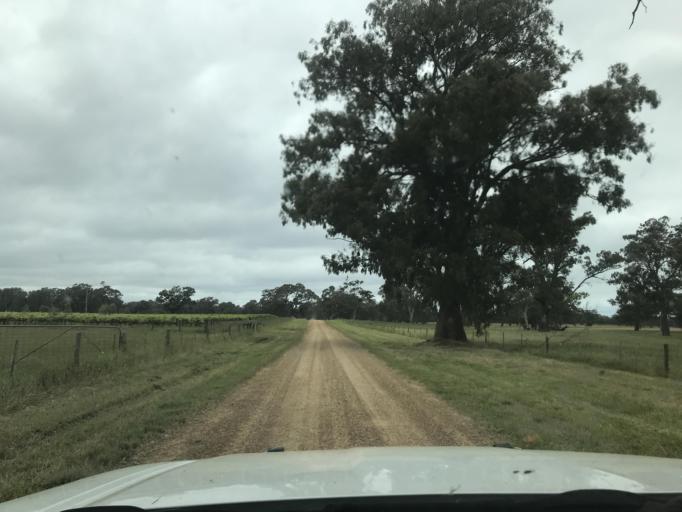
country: AU
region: South Australia
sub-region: Wattle Range
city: Penola
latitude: -37.2748
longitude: 140.9852
